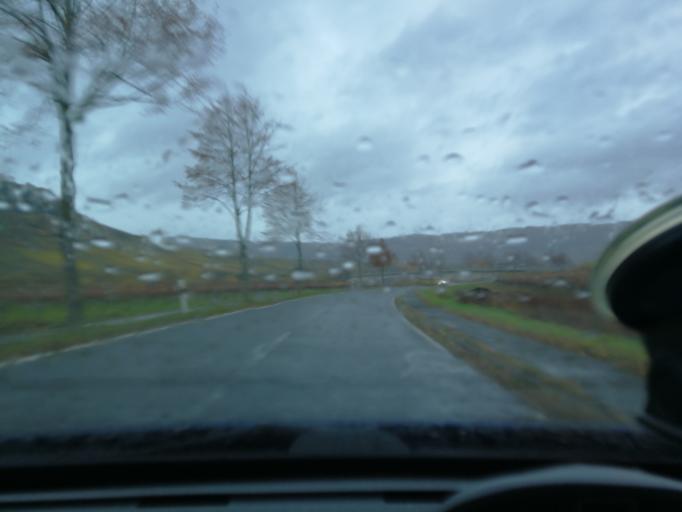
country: DE
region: Rheinland-Pfalz
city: Minheim
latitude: 49.8644
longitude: 6.9314
